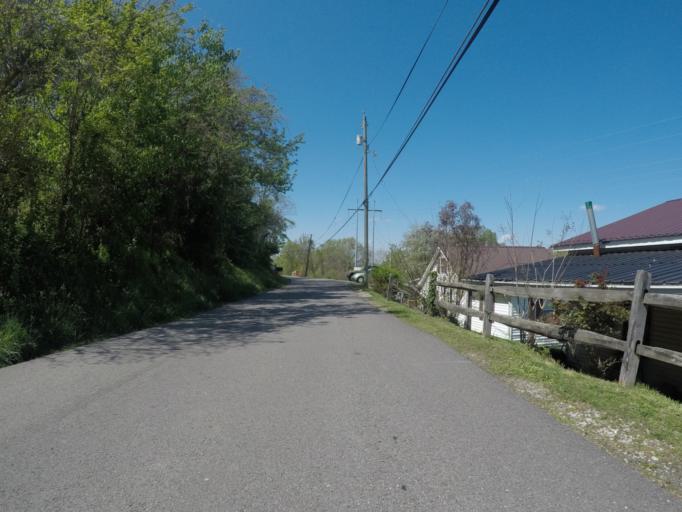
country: US
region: West Virginia
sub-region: Wayne County
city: Kenova
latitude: 38.3930
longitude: -82.5844
